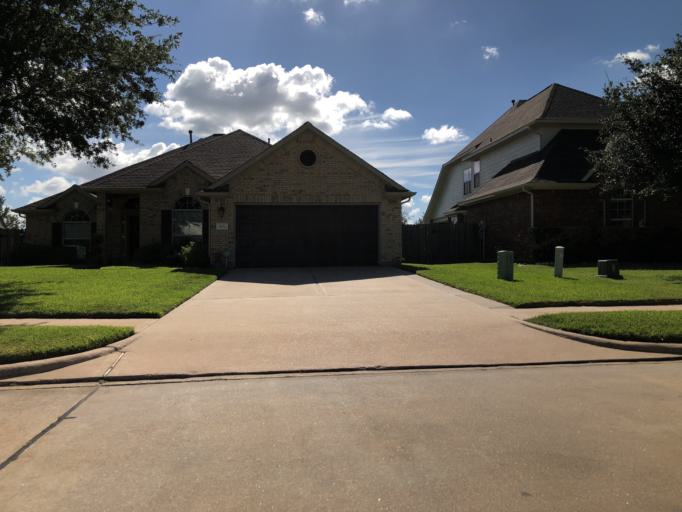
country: US
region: Texas
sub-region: Harris County
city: Katy
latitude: 29.8070
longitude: -95.8330
